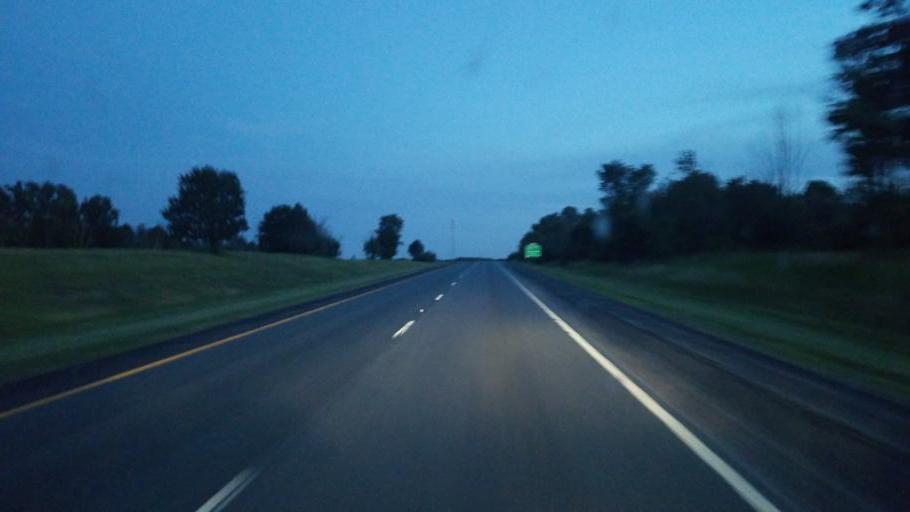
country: US
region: Ohio
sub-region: Medina County
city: Brunswick
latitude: 41.1759
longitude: -81.7611
